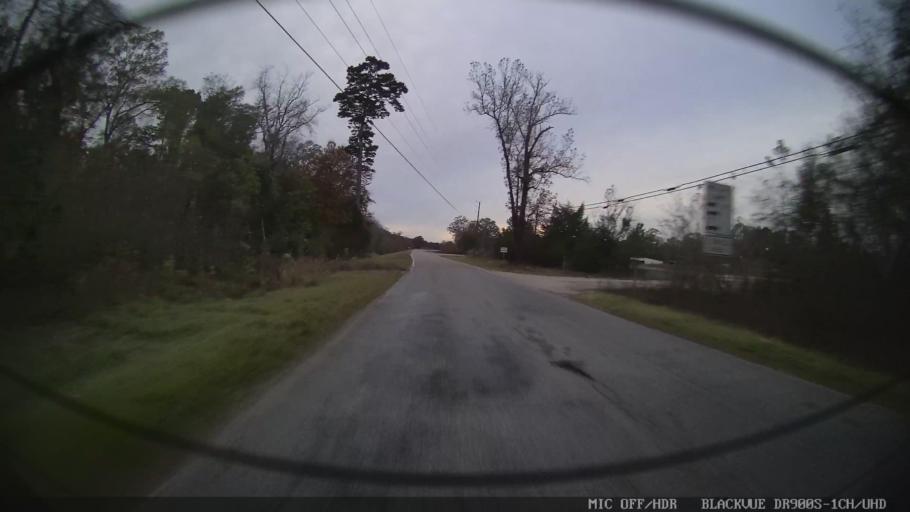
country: US
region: Mississippi
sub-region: Clarke County
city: Quitman
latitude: 32.0421
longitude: -88.7375
